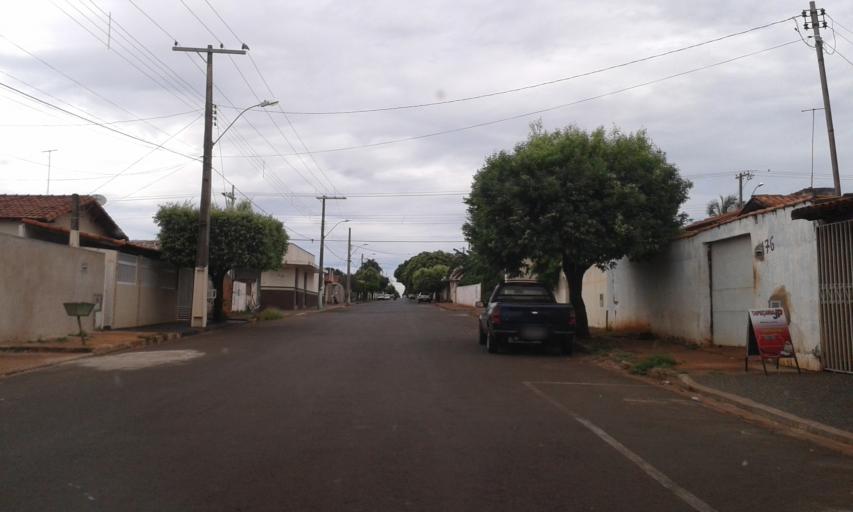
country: BR
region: Minas Gerais
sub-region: Ituiutaba
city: Ituiutaba
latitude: -18.9807
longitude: -49.4489
